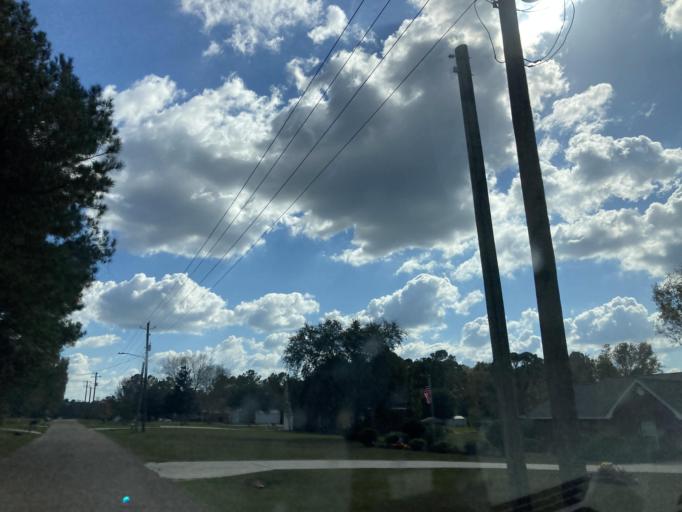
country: US
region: Mississippi
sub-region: Lamar County
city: Sumrall
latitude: 31.3957
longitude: -89.5404
